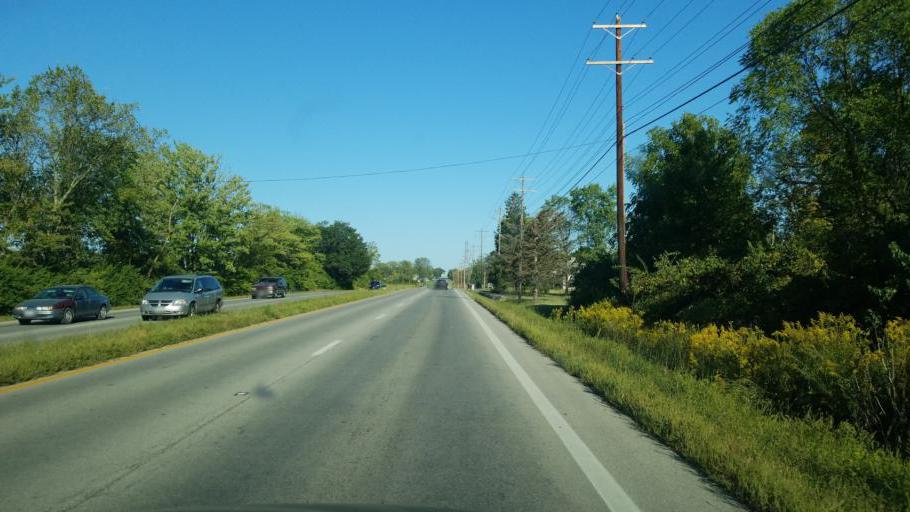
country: US
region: Ohio
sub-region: Franklin County
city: Lake Darby
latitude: 39.9495
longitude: -83.1901
